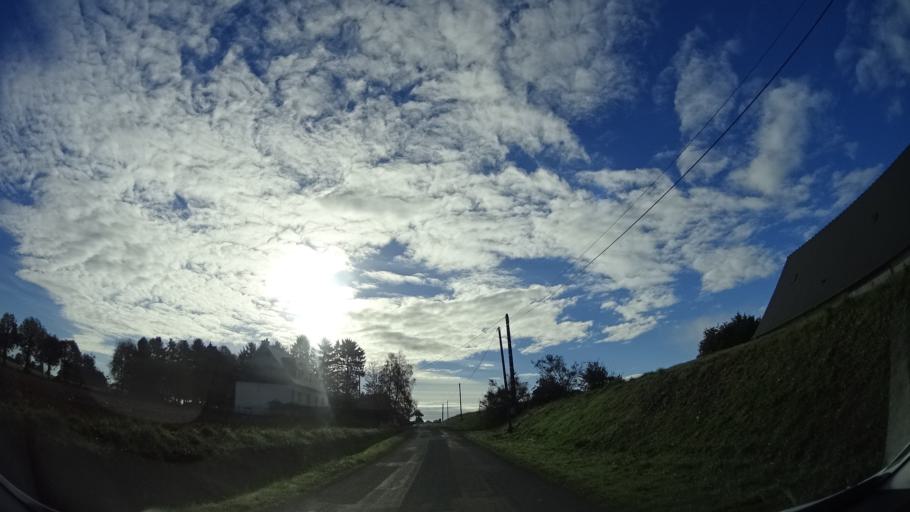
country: FR
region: Brittany
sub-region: Departement d'Ille-et-Vilaine
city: Geveze
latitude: 48.1934
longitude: -1.8179
